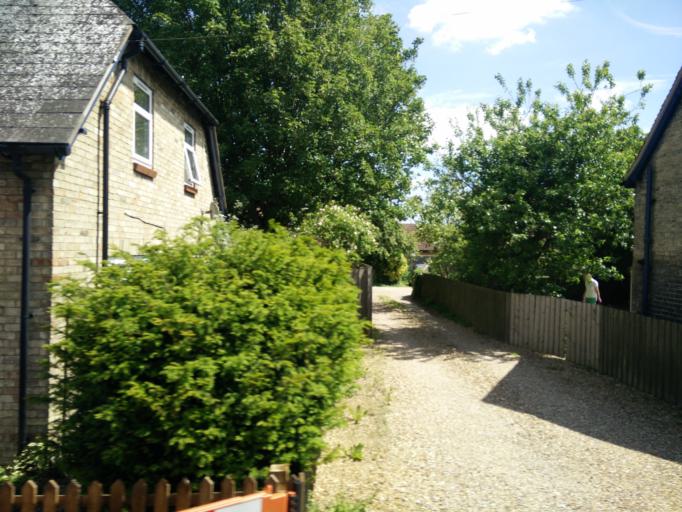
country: GB
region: England
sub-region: Cambridgeshire
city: Grantchester
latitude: 52.1740
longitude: 0.1128
